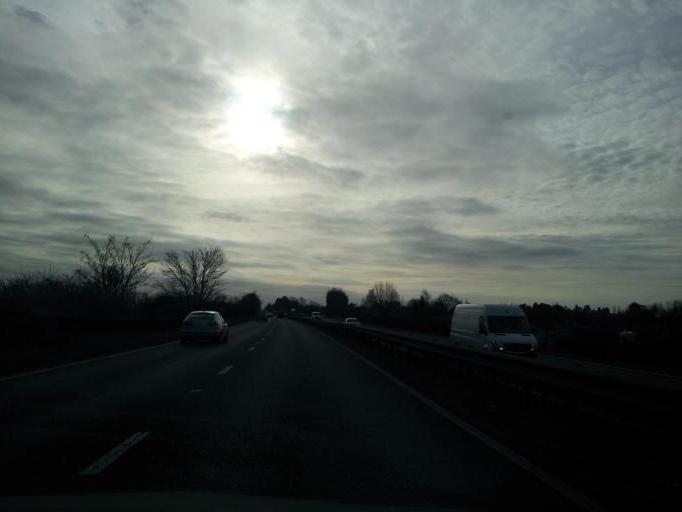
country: GB
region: England
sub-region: Peterborough
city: Wittering
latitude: 52.6174
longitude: -0.4497
